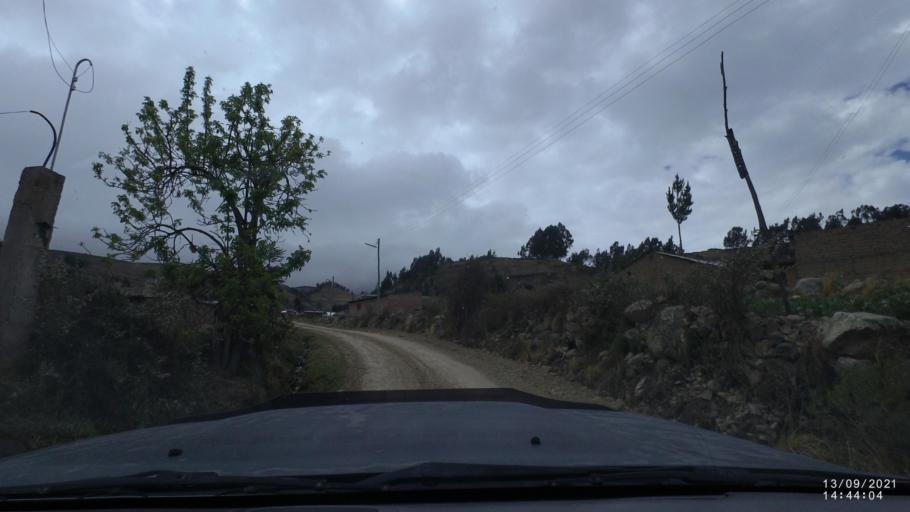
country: BO
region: Cochabamba
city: Colomi
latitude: -17.3604
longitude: -65.8118
